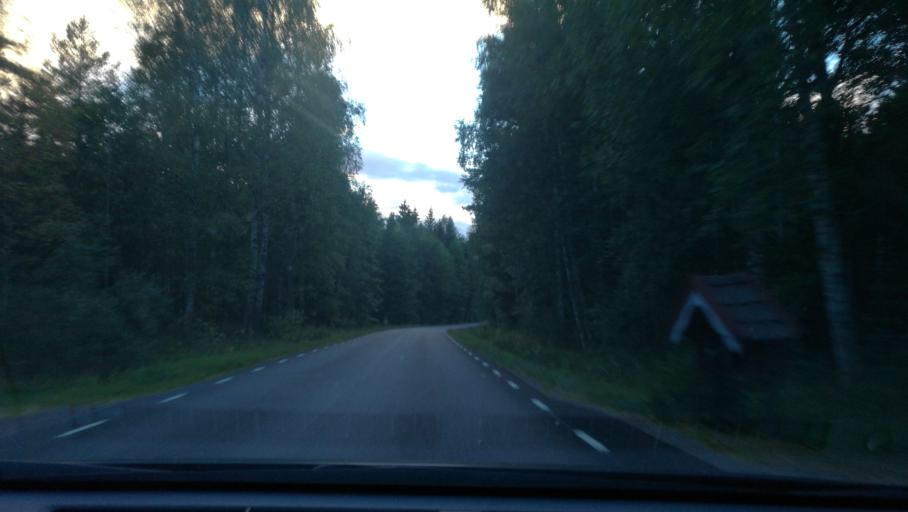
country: SE
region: OEstergoetland
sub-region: Norrkopings Kommun
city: Jursla
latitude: 58.8117
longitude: 16.0901
